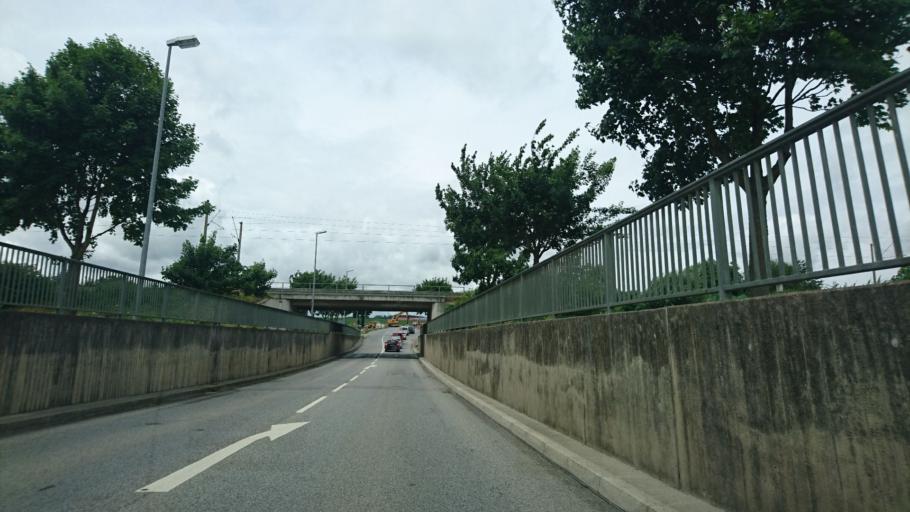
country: DE
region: Bavaria
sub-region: Lower Bavaria
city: Ergolding
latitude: 48.5690
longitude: 12.1538
